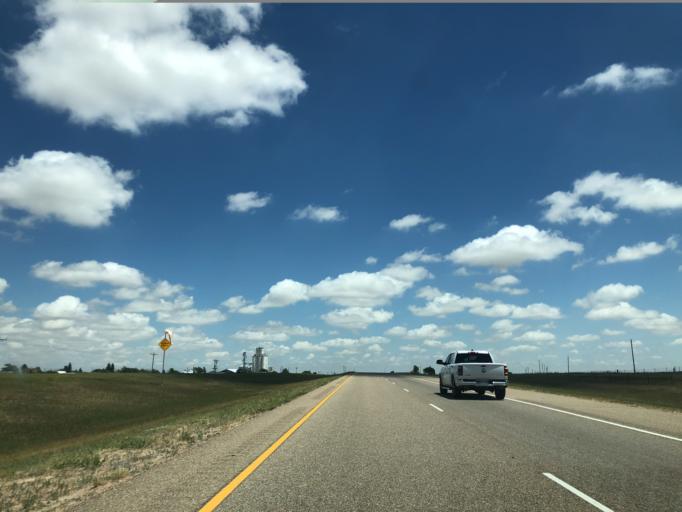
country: US
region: Colorado
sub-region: Lincoln County
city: Hugo
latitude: 39.2728
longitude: -103.5069
